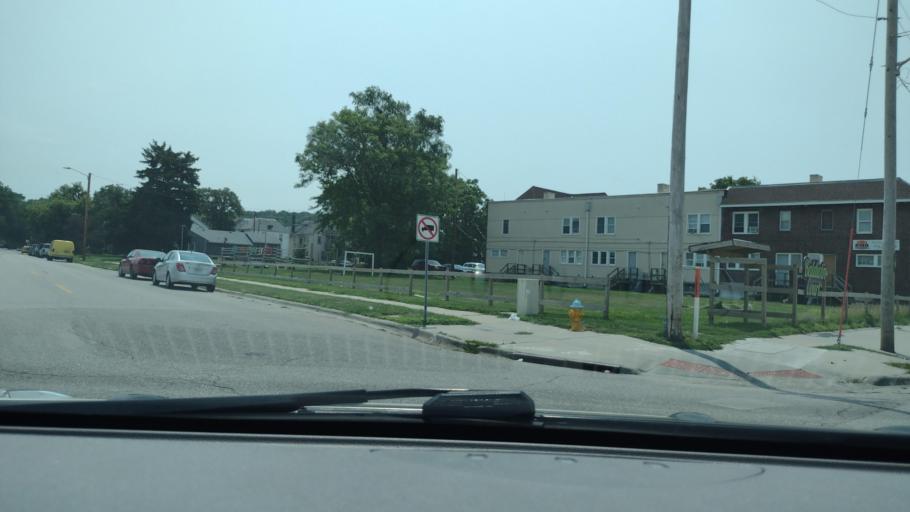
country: US
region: Iowa
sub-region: Pottawattamie County
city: Council Bluffs
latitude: 41.2606
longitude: -95.8561
